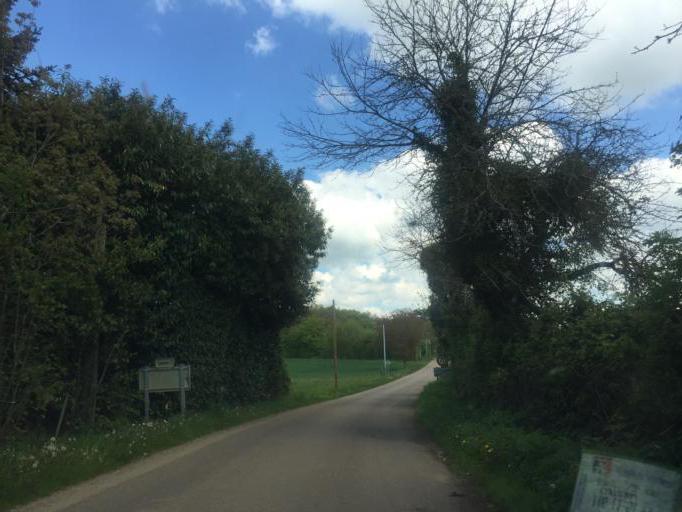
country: FR
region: Bourgogne
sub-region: Departement de l'Yonne
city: Fontenailles
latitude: 47.5441
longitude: 3.3370
